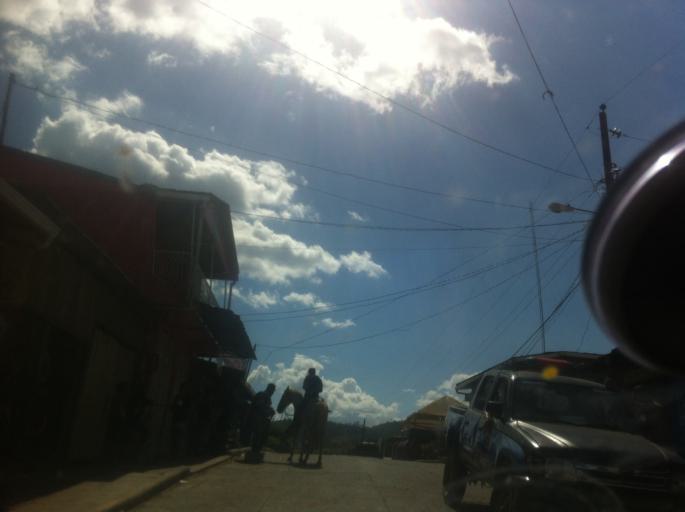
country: NI
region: Rio San Juan
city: San Carlos
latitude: 11.2366
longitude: -84.5597
